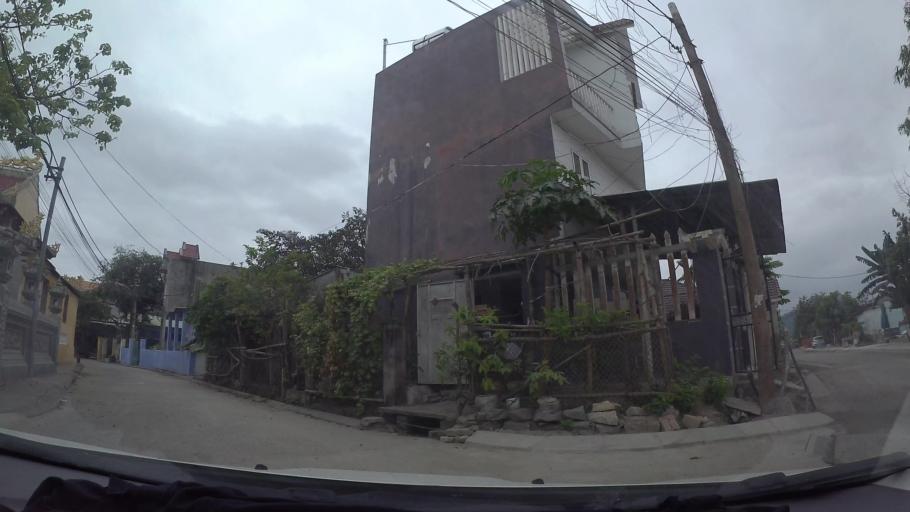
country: VN
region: Da Nang
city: Lien Chieu
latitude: 16.1042
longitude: 108.1300
